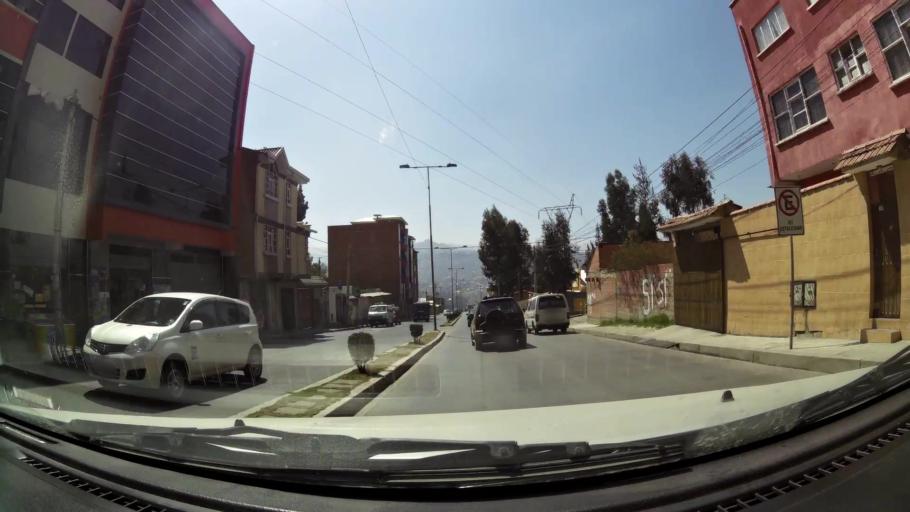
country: BO
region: La Paz
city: La Paz
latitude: -16.5309
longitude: -68.1261
